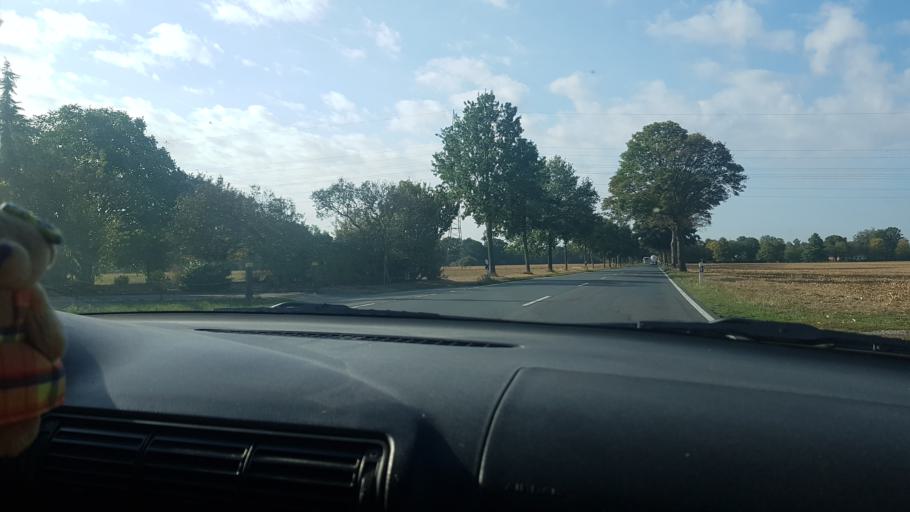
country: DE
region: Lower Saxony
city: Drakenburg
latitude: 52.6837
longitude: 9.2309
